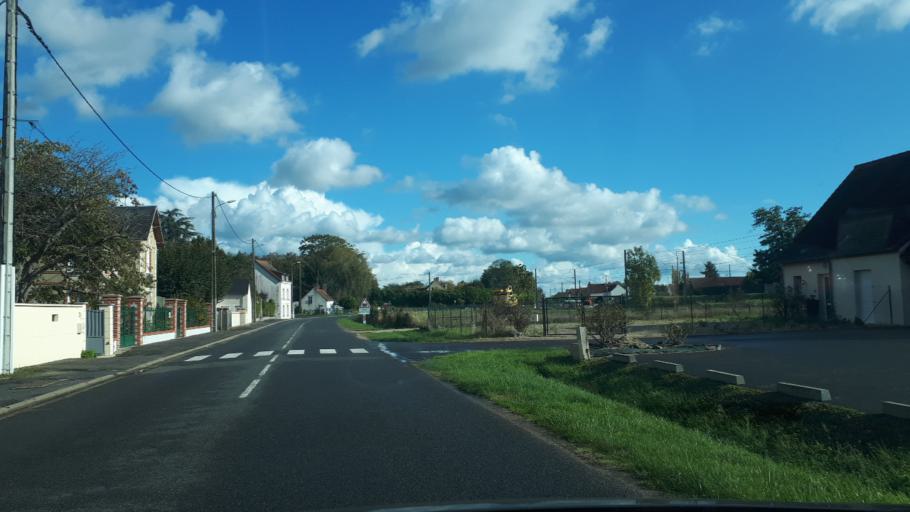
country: FR
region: Centre
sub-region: Departement du Loir-et-Cher
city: Thesee
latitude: 47.3222
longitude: 1.3140
